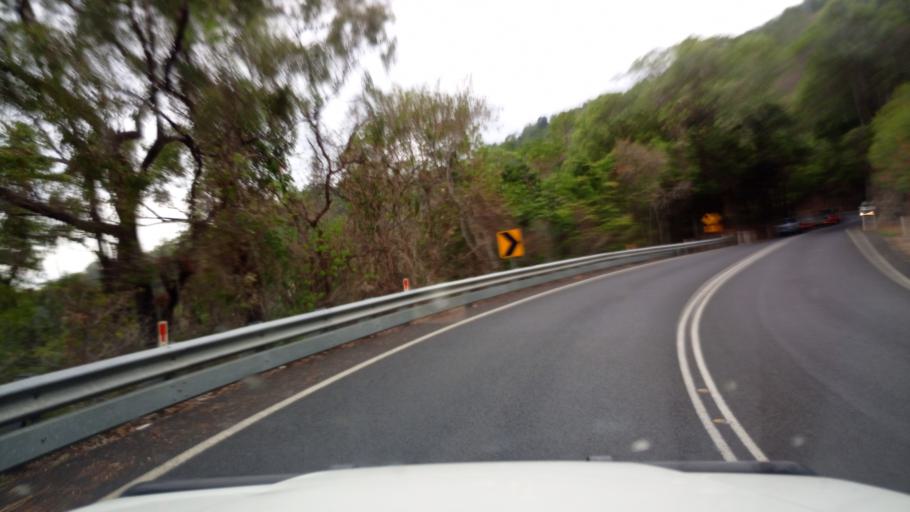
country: AU
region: Queensland
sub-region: Cairns
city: Redlynch
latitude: -16.8453
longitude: 145.6828
